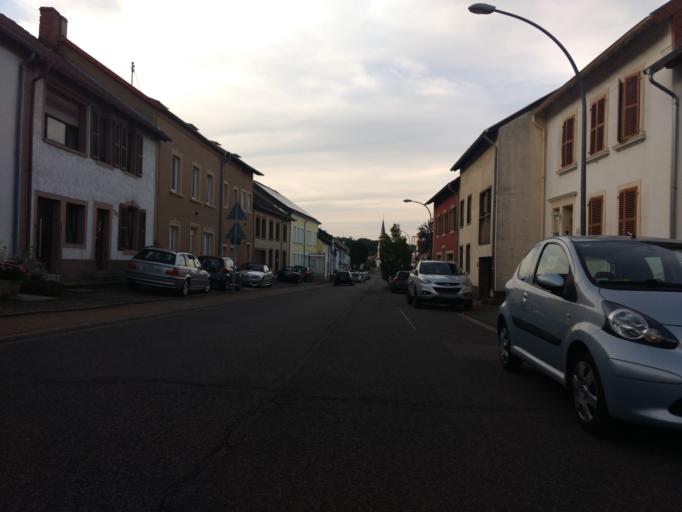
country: DE
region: Saarland
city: Wallerfangen
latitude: 49.3146
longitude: 6.7221
